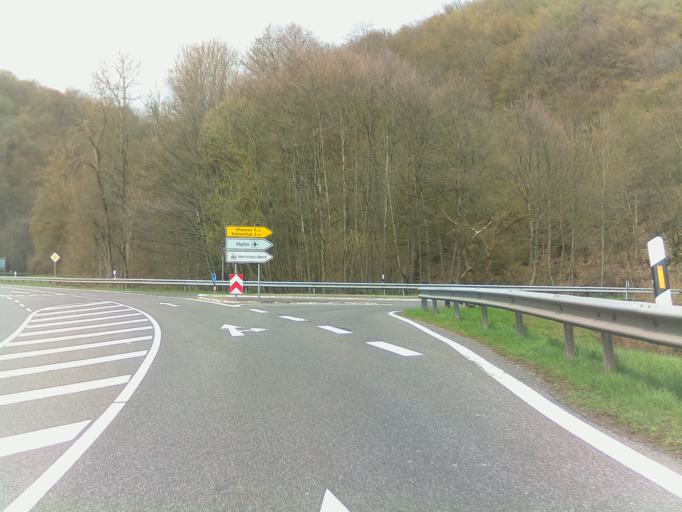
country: DE
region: Rheinland-Pfalz
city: Morschied
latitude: 49.7908
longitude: 7.3239
